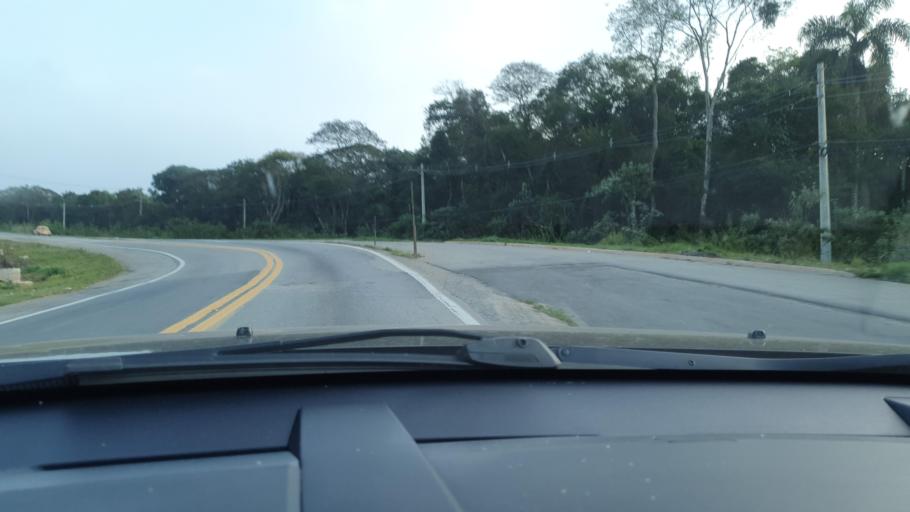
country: BR
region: Sao Paulo
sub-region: Vargem Grande Paulista
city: Vargem Grande Paulista
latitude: -23.6568
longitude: -47.0874
